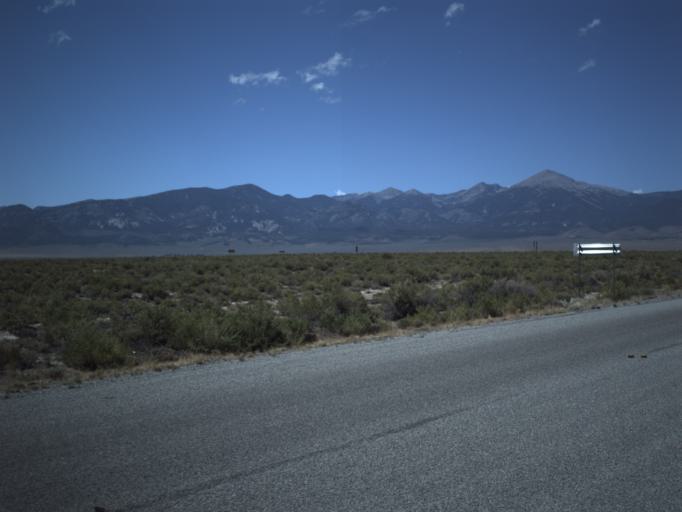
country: US
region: Nevada
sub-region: White Pine County
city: McGill
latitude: 39.0561
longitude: -114.0344
